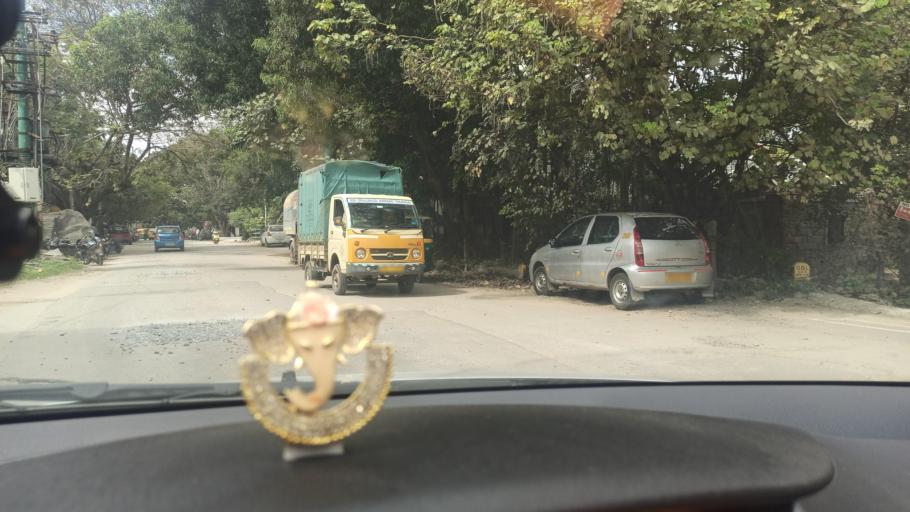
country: IN
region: Karnataka
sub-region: Bangalore Urban
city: Bangalore
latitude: 12.9142
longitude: 77.6279
